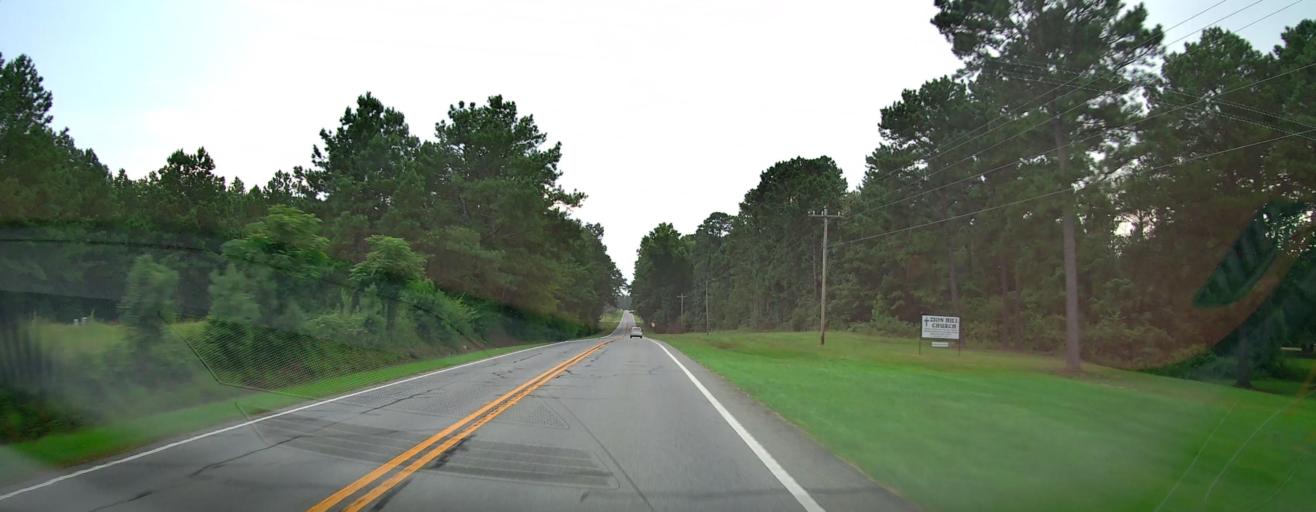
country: US
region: Georgia
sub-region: Laurens County
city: East Dublin
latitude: 32.5859
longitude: -82.8335
